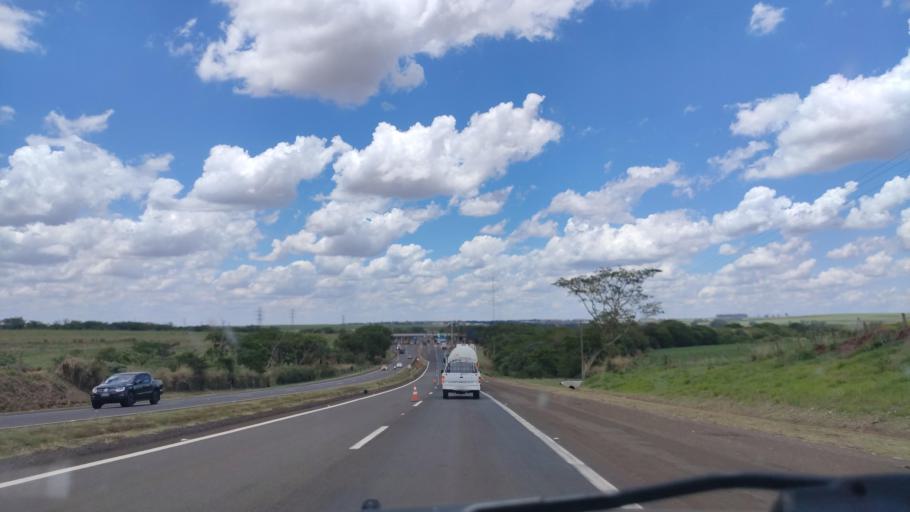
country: BR
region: Sao Paulo
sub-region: Pederneiras
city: Pederneiras
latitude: -22.3151
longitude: -48.7213
